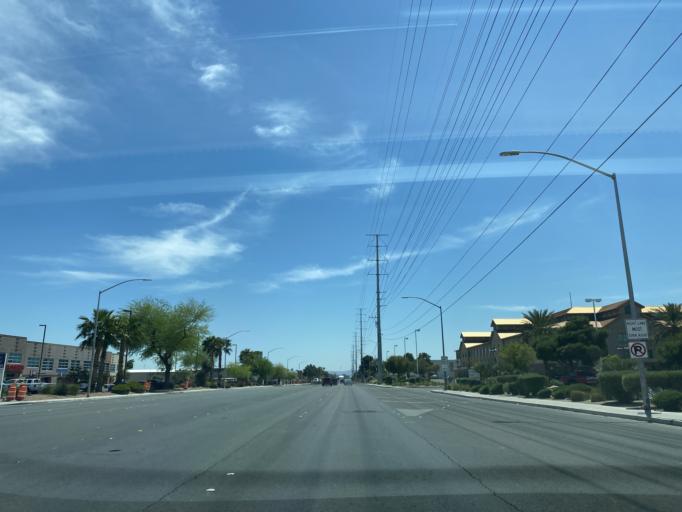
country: US
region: Nevada
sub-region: Clark County
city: North Las Vegas
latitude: 36.2394
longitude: -115.1169
